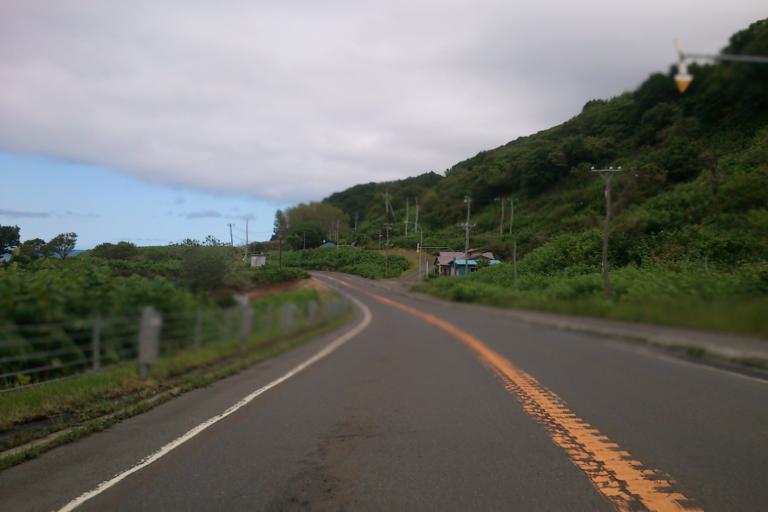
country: JP
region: Hokkaido
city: Ishikari
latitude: 43.4212
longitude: 141.4291
